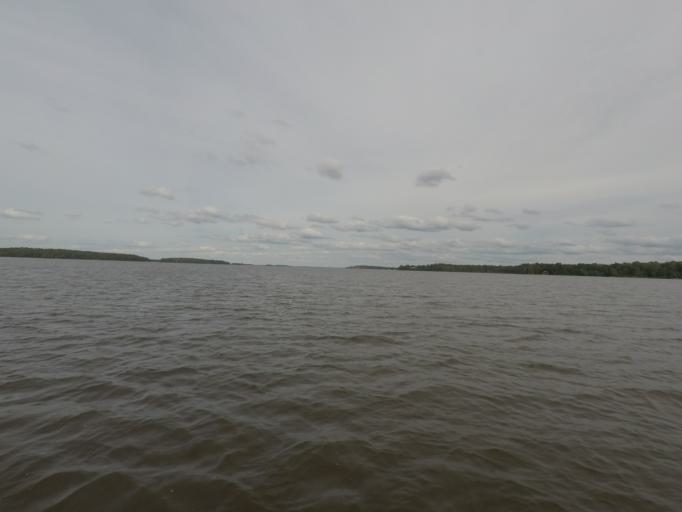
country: SE
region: Soedermanland
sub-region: Eskilstuna Kommun
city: Kvicksund
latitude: 59.4564
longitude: 16.3755
